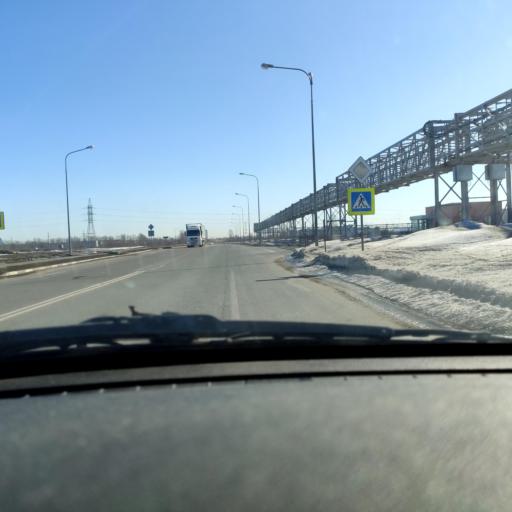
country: RU
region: Samara
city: Podstepki
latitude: 53.5597
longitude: 49.1998
